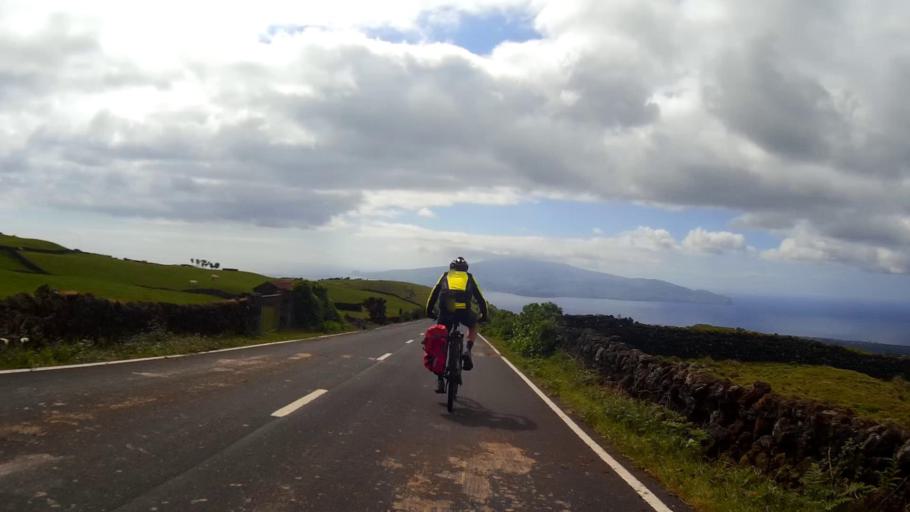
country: PT
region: Azores
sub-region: Madalena
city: Madalena
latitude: 38.4956
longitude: -28.4558
